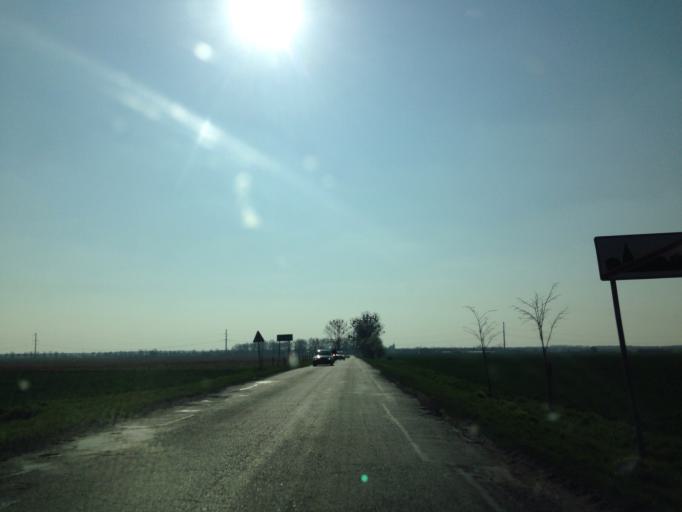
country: PL
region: Lower Silesian Voivodeship
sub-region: Powiat wroclawski
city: Kielczow
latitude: 51.1447
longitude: 17.2122
